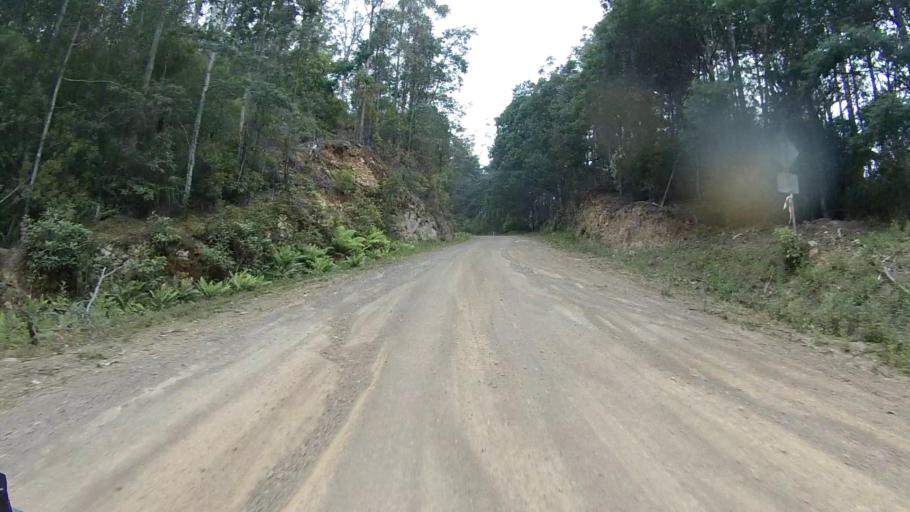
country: AU
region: Tasmania
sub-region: Sorell
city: Sorell
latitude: -42.7065
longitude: 147.8510
